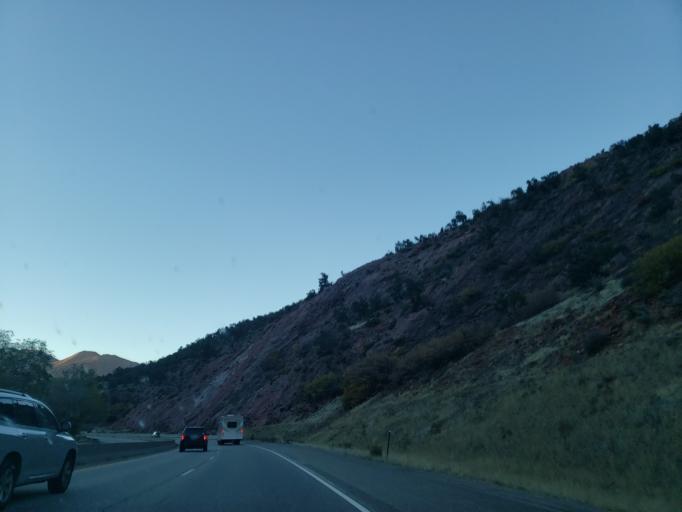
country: US
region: Colorado
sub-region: Garfield County
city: Glenwood Springs
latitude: 39.5694
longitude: -107.4272
